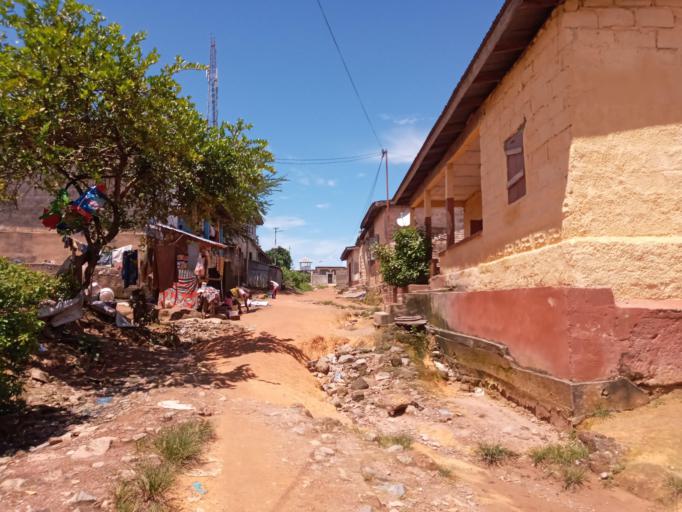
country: SL
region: Eastern Province
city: Koidu
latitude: 8.6396
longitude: -10.9731
